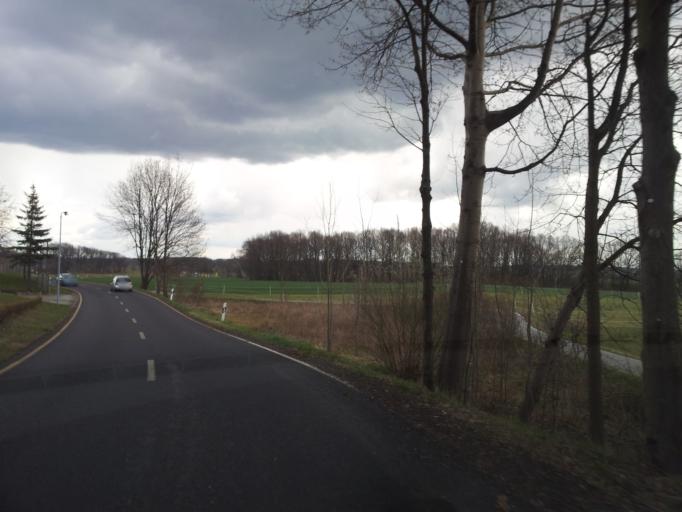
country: DE
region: Saxony
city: Panschwitz-Kuckau
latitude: 51.2564
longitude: 14.2043
